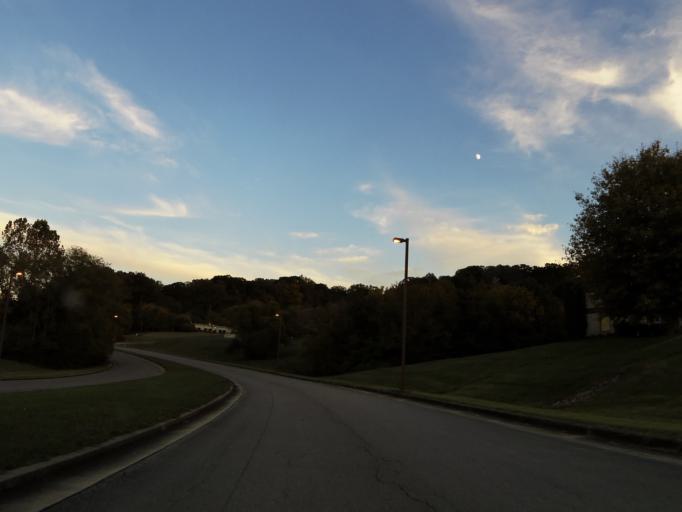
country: US
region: Tennessee
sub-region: Blount County
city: Eagleton Village
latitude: 35.8616
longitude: -83.9381
